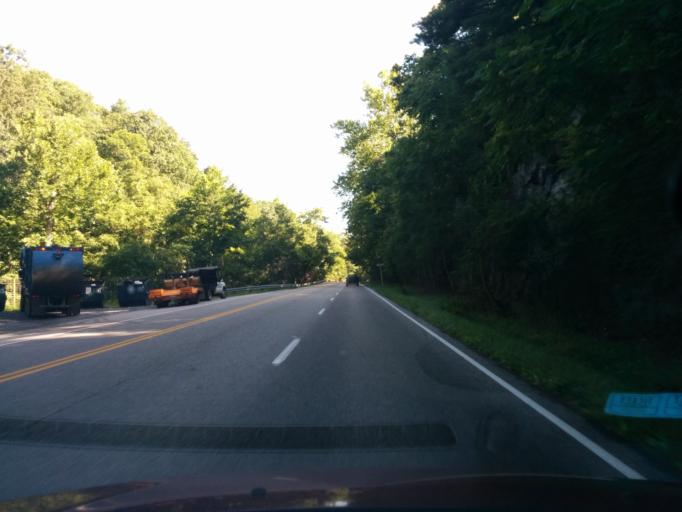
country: US
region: Virginia
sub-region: City of Lexington
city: Lexington
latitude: 37.7214
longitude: -79.4701
